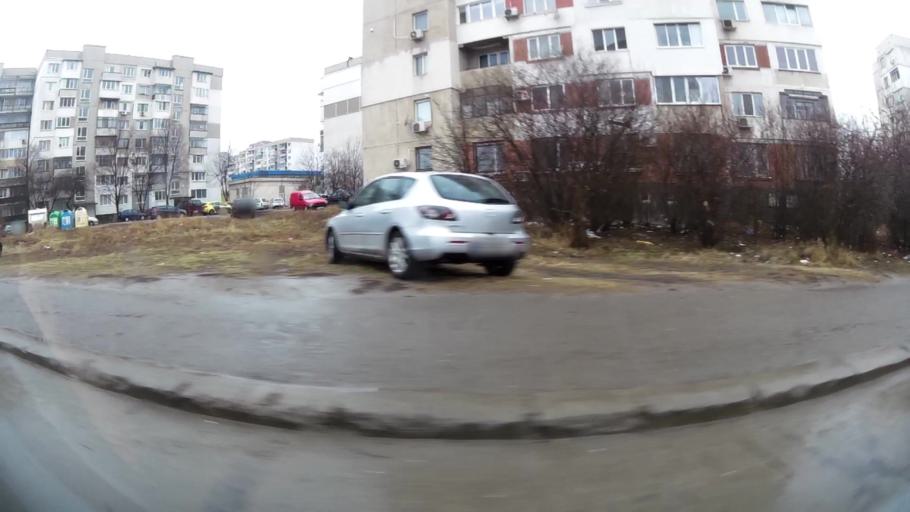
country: BG
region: Sofia-Capital
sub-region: Stolichna Obshtina
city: Sofia
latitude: 42.6296
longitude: 23.3824
